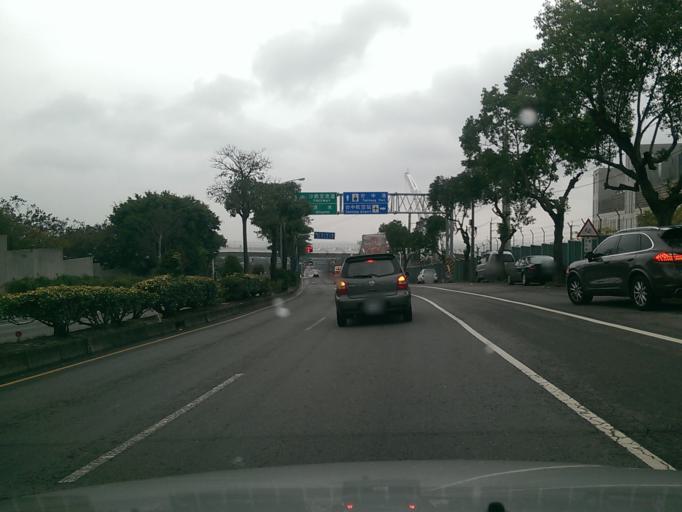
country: TW
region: Taiwan
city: Fengyuan
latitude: 24.2501
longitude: 120.5999
